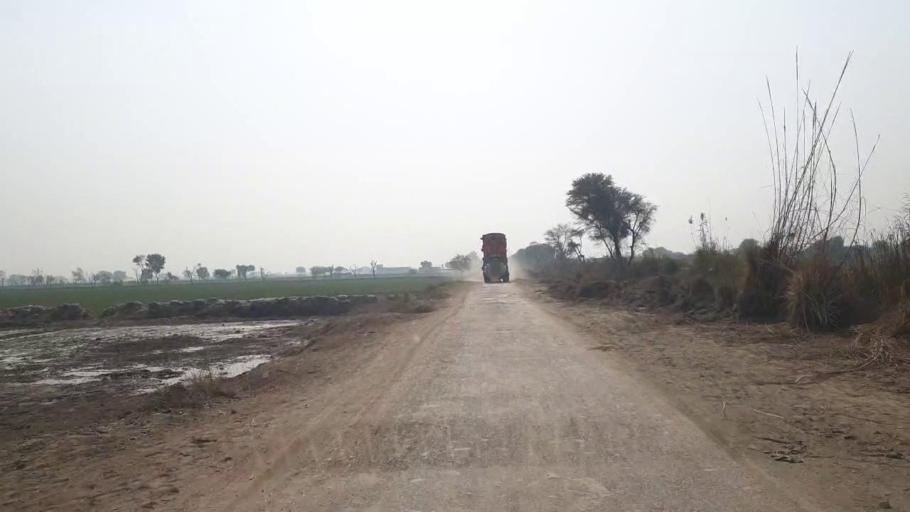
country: PK
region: Sindh
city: Hala
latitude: 25.9138
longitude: 68.4460
